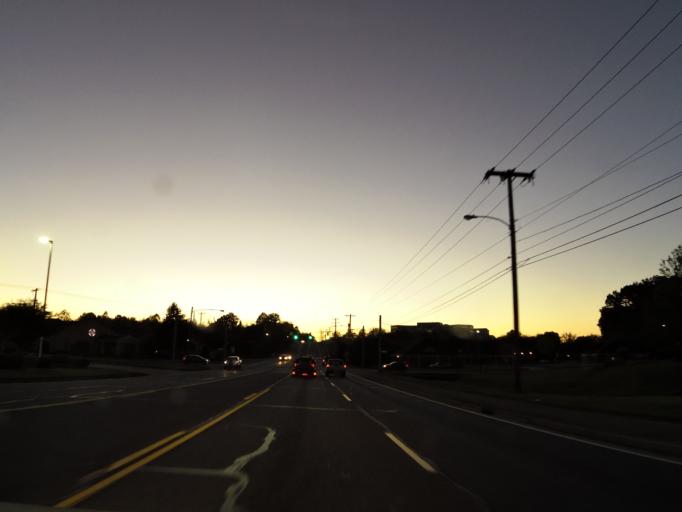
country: US
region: Tennessee
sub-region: Blount County
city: Maryville
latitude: 35.7552
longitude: -83.9513
